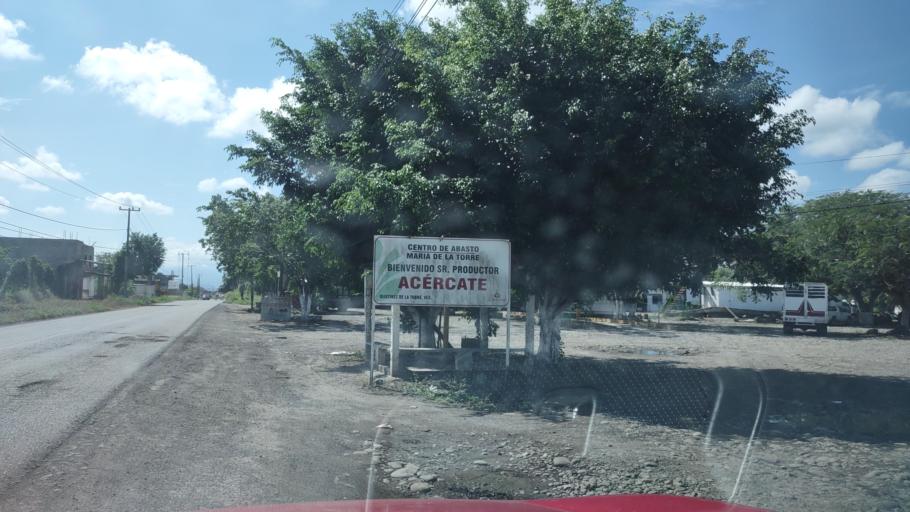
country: MX
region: Veracruz
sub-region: Martinez de la Torre
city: La Union Paso Largo
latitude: 20.1330
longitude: -96.9972
